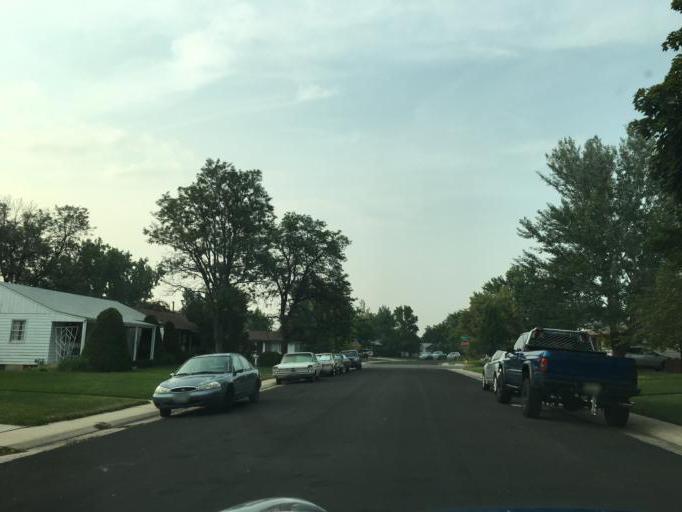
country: US
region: Colorado
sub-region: Arapahoe County
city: Glendale
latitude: 39.6849
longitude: -104.9296
